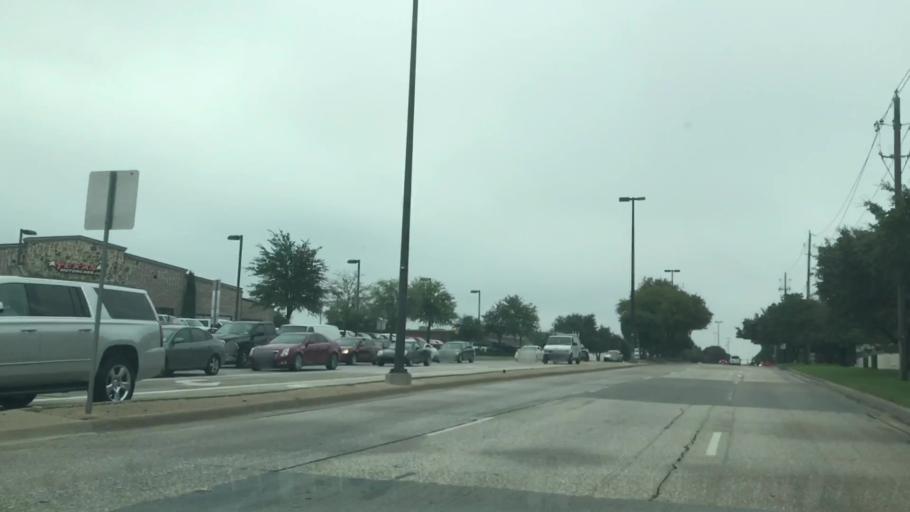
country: US
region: Texas
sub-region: Dallas County
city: Addison
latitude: 32.9688
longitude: -96.8418
